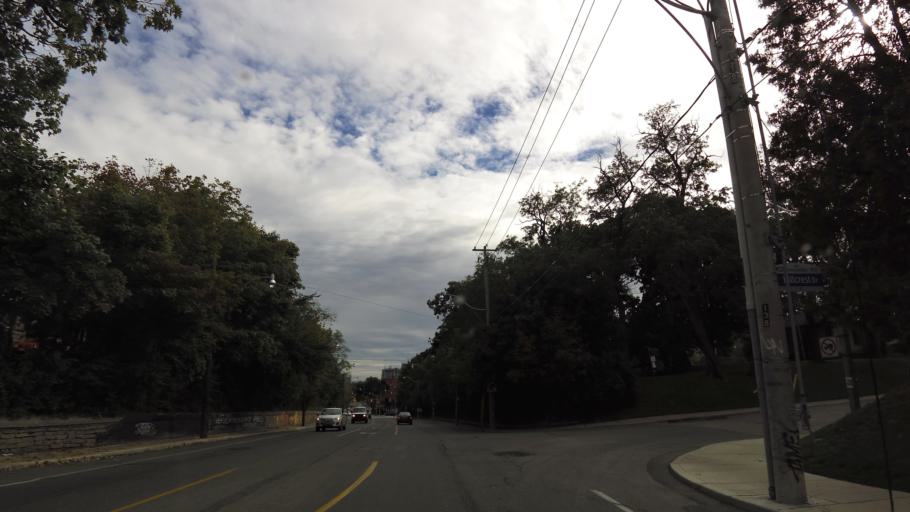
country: CA
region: Ontario
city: Toronto
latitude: 43.6770
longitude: -79.4236
